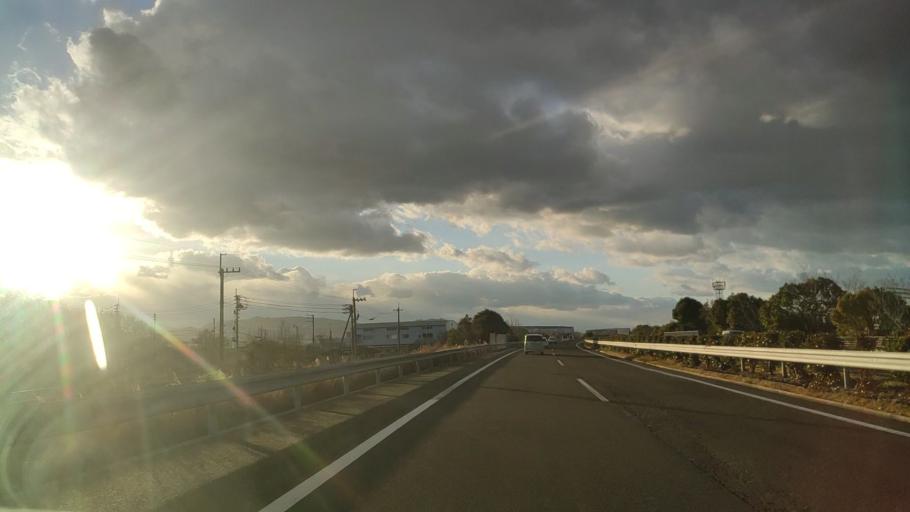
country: JP
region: Ehime
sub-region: Shikoku-chuo Shi
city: Matsuyama
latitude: 33.7848
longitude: 132.8487
